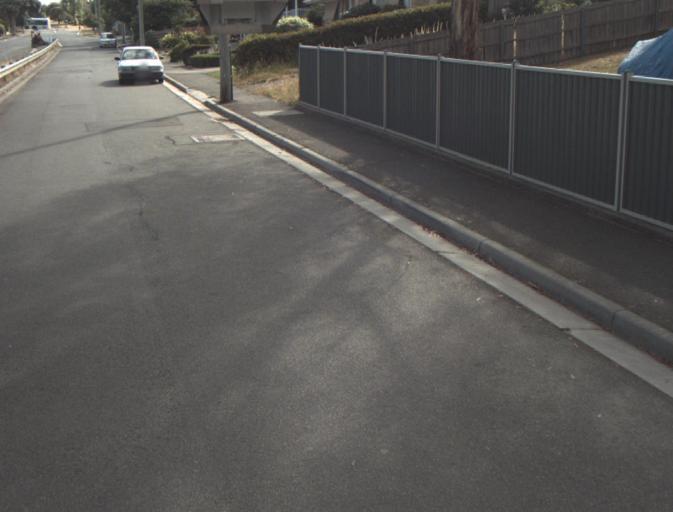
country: AU
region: Tasmania
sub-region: Launceston
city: Summerhill
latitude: -41.4608
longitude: 147.1266
